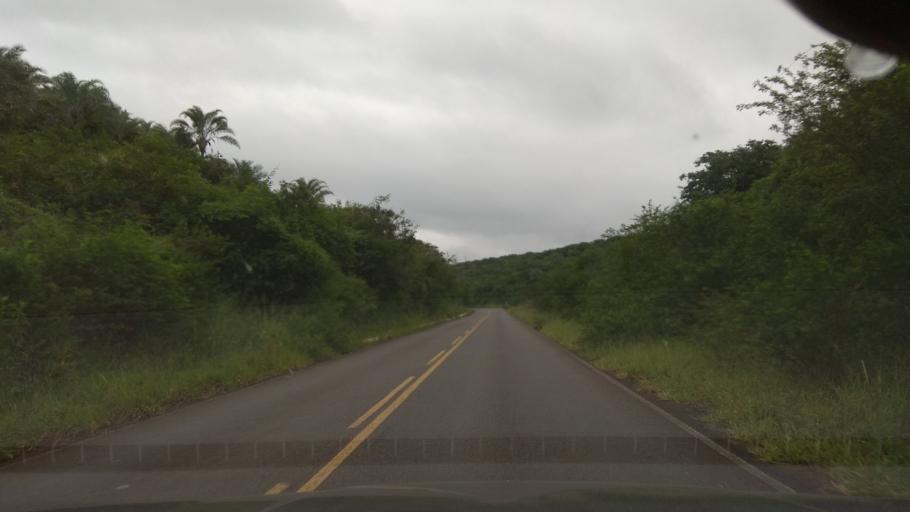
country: BR
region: Bahia
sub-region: Santa Ines
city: Santa Ines
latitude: -13.2606
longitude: -39.7834
